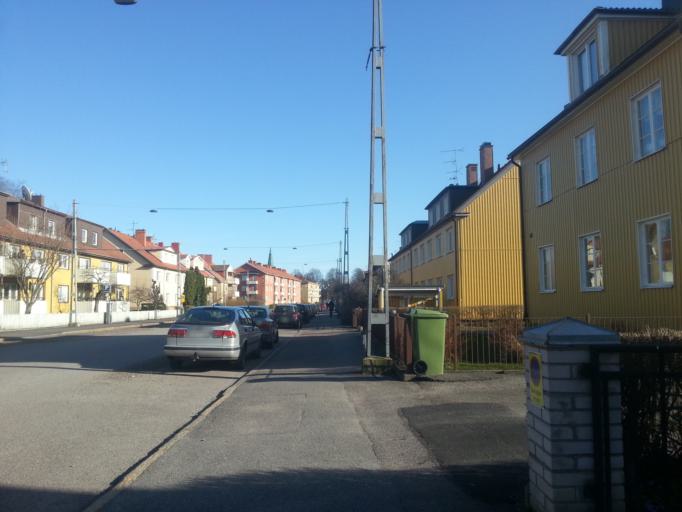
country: SE
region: OEstergoetland
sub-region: Norrkopings Kommun
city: Norrkoping
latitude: 58.5794
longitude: 16.1913
